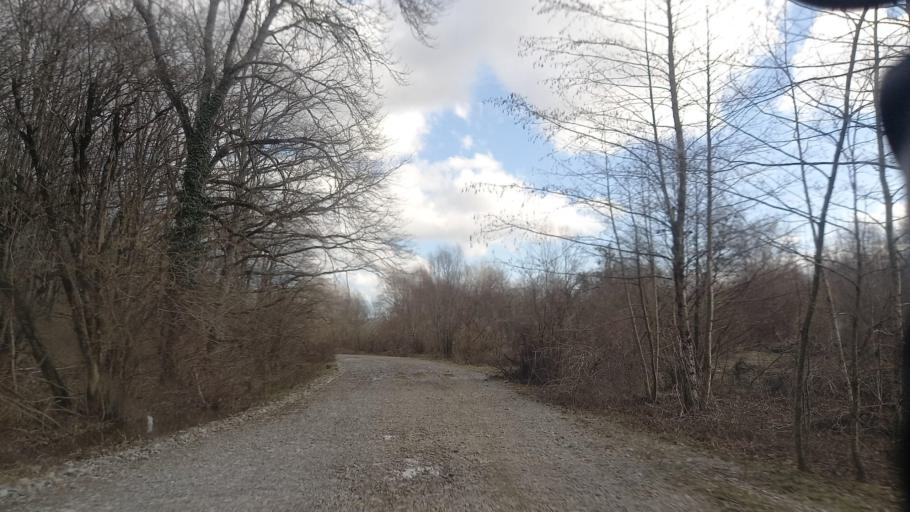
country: RU
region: Krasnodarskiy
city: Smolenskaya
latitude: 44.6058
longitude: 38.8388
